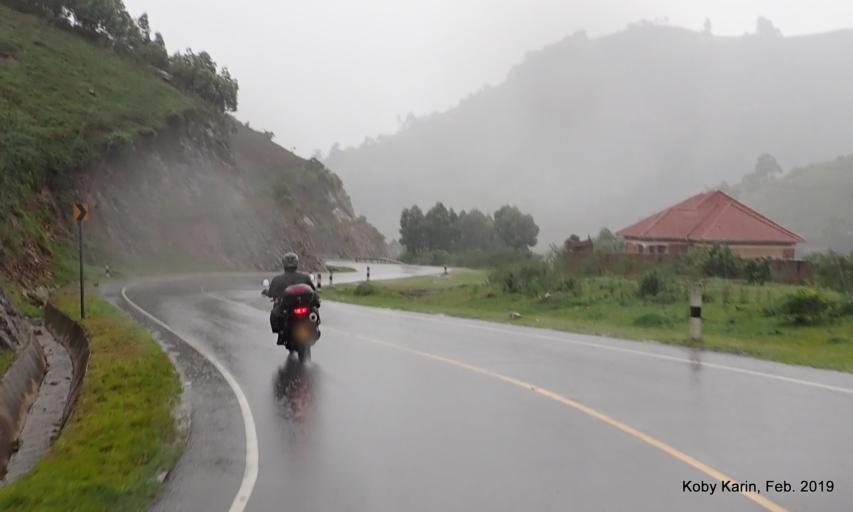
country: UG
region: Western Region
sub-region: Kisoro District
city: Kisoro
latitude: -1.2558
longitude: 29.7799
